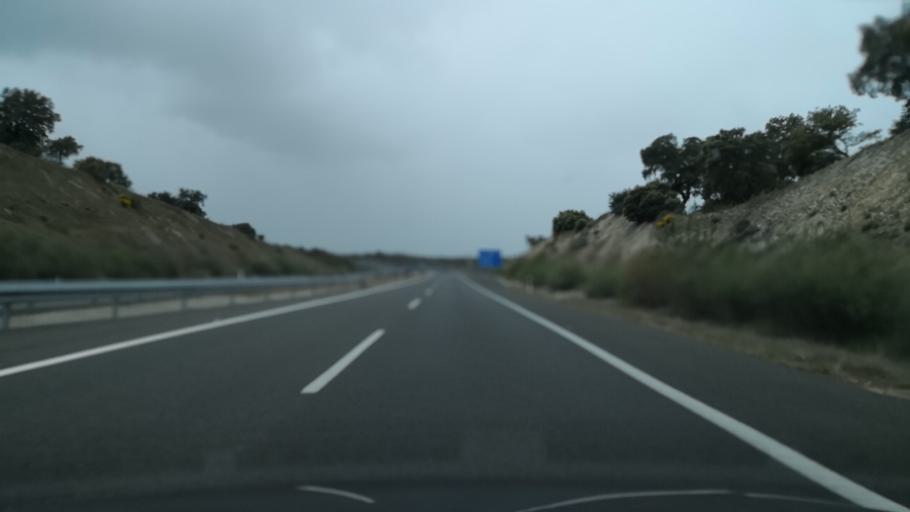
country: ES
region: Extremadura
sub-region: Provincia de Caceres
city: Plasencia
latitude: 40.0608
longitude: -6.1227
